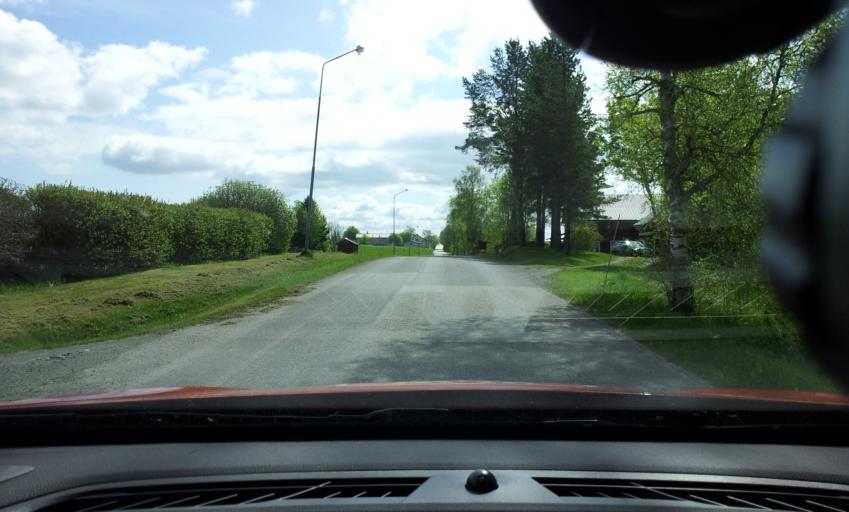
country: SE
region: Jaemtland
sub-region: OEstersunds Kommun
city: Ostersund
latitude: 63.0131
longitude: 14.6010
